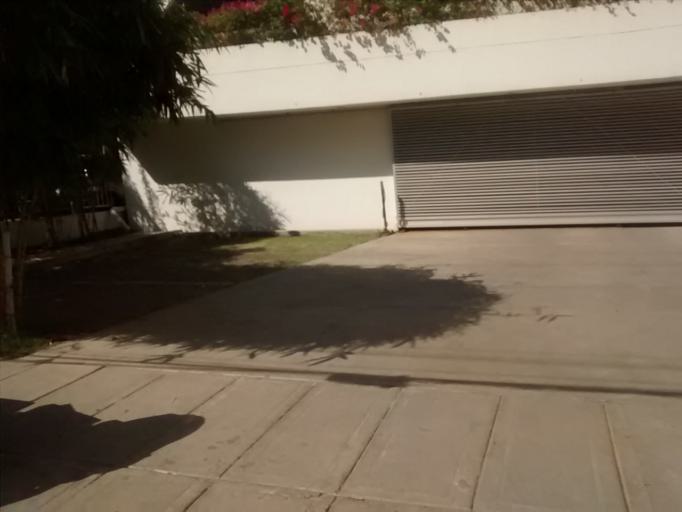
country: CO
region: Bolivar
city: Cartagena
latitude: 10.3963
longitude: -75.5544
